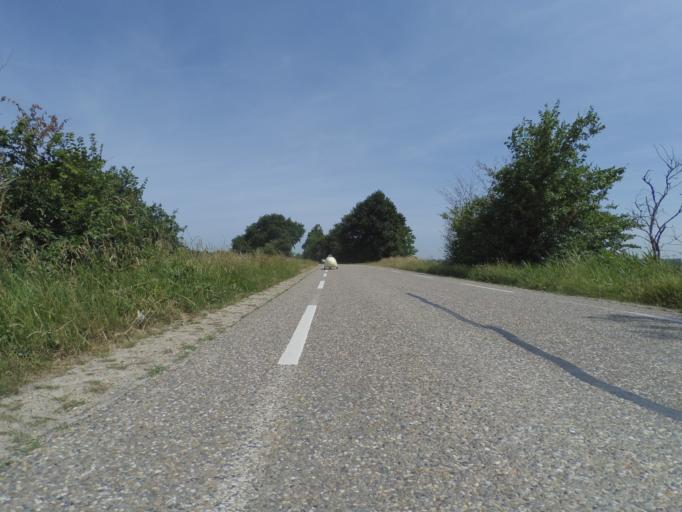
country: NL
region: North Brabant
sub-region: Gemeente Steenbergen
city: Nieuw-Vossemeer
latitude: 51.5703
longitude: 4.1510
